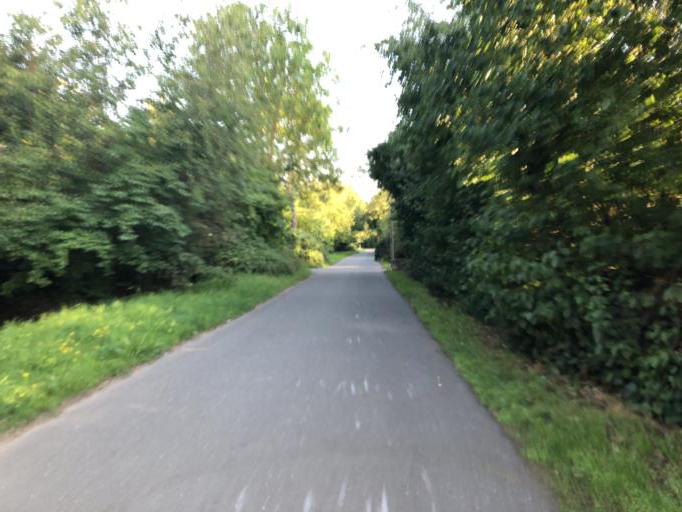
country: DE
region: Bavaria
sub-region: Regierungsbezirk Mittelfranken
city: Erlangen
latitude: 49.5942
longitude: 10.9553
